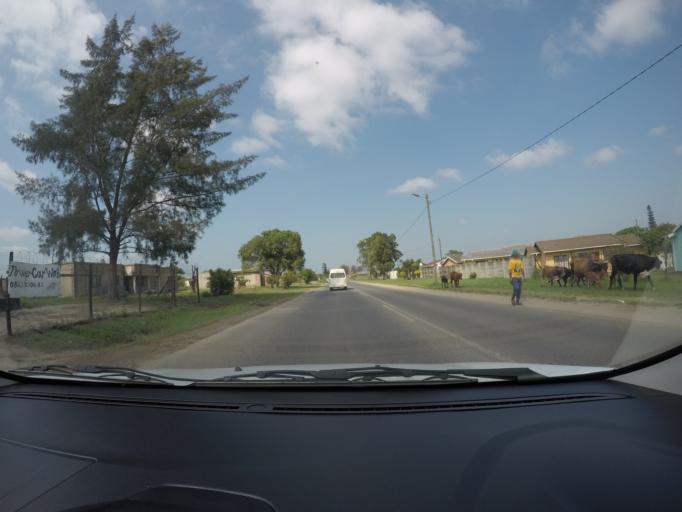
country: ZA
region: KwaZulu-Natal
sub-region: uThungulu District Municipality
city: eSikhawini
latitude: -28.8865
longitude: 31.8987
